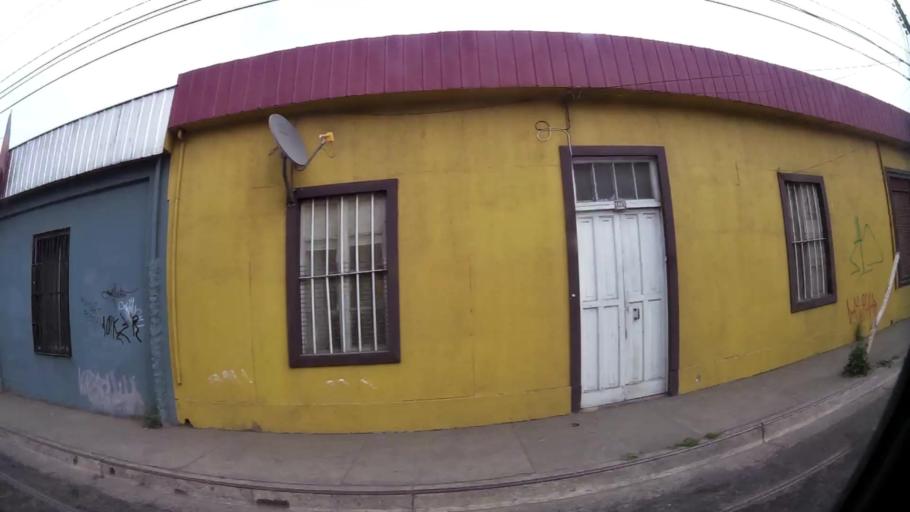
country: CL
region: Santiago Metropolitan
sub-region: Provincia de Santiago
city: Santiago
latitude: -33.4614
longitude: -70.6532
